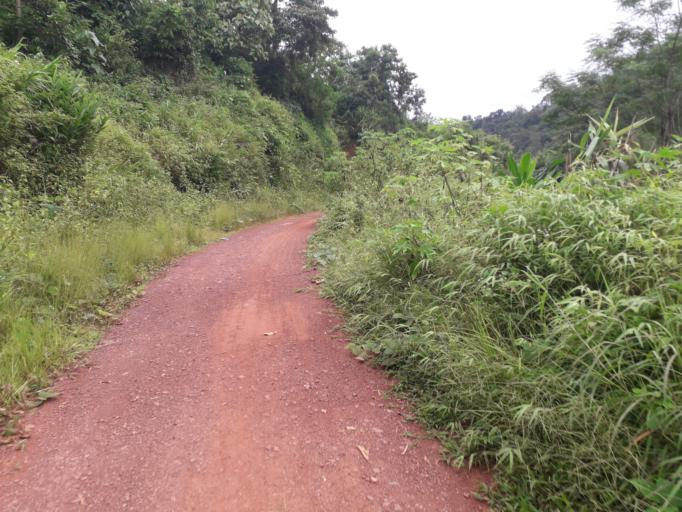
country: CN
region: Yunnan
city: Menglie
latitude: 22.2029
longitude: 101.6721
